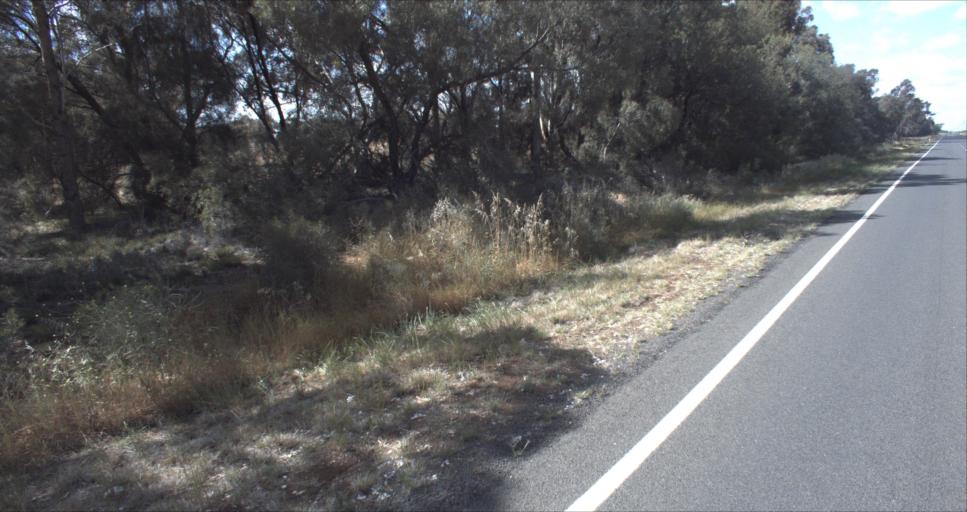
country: AU
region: New South Wales
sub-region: Murrumbidgee Shire
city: Darlington Point
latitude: -34.5299
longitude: 146.1741
